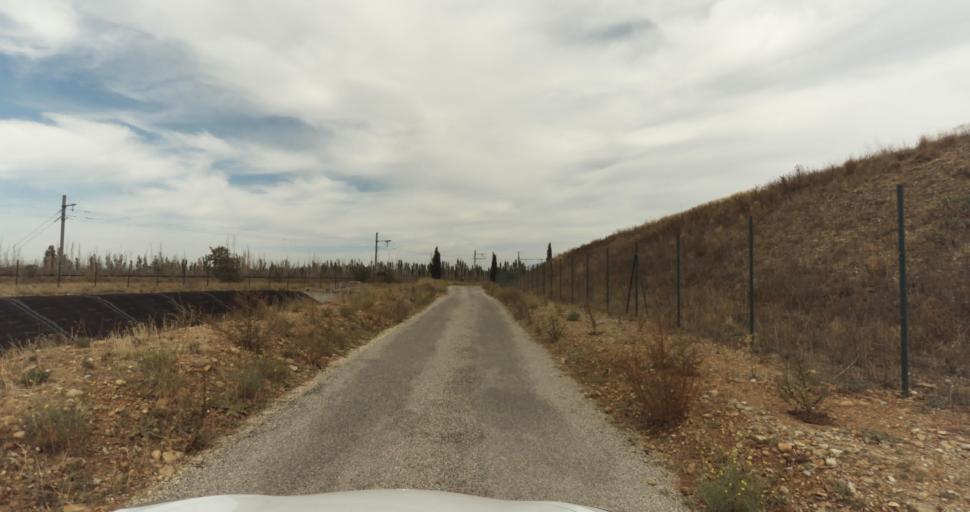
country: FR
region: Provence-Alpes-Cote d'Azur
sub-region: Departement des Bouches-du-Rhone
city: Miramas
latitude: 43.6004
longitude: 4.9897
